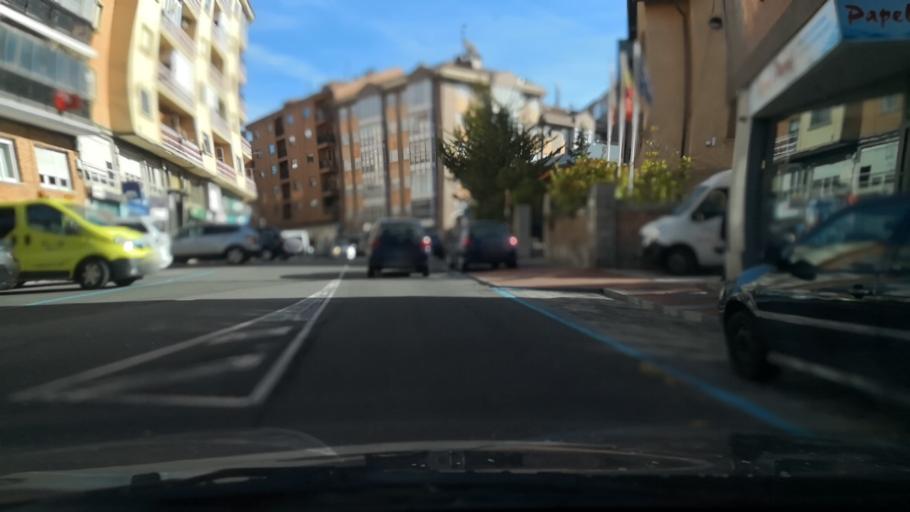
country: ES
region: Castille and Leon
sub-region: Provincia de Avila
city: Avila
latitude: 40.6533
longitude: -4.6869
